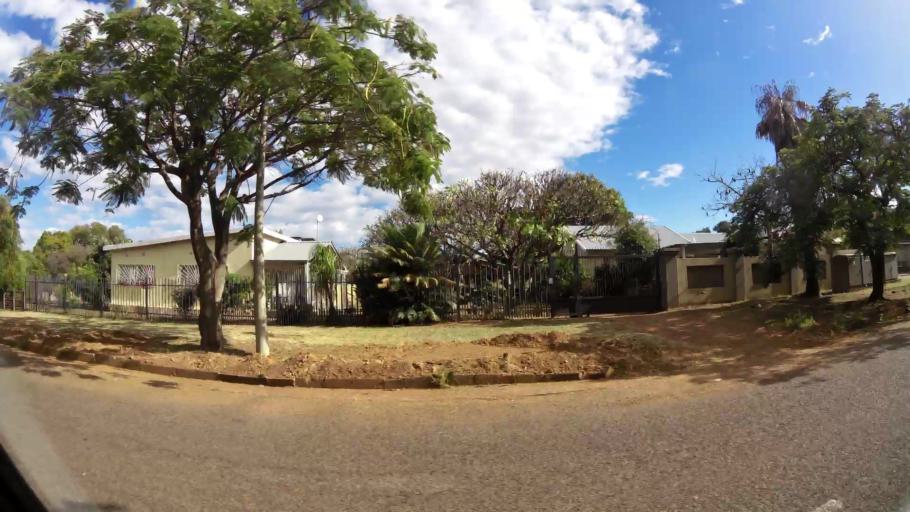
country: ZA
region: Limpopo
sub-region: Waterberg District Municipality
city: Warmbaths
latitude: -24.8788
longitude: 28.2885
